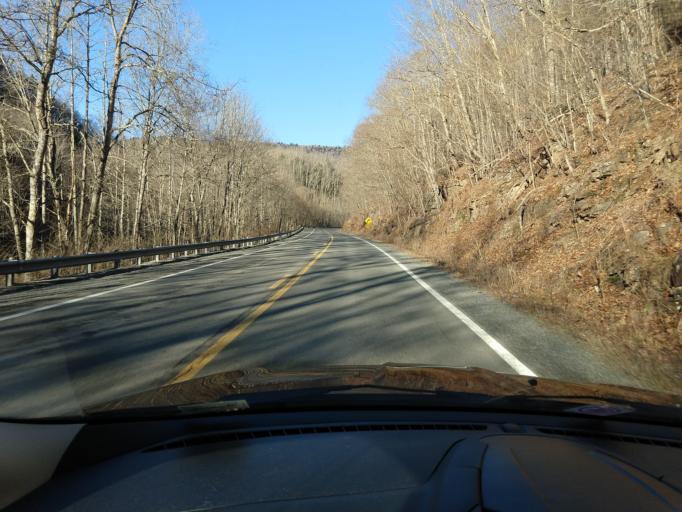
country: US
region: Virginia
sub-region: Highland County
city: Monterey
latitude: 38.5603
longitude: -79.8356
